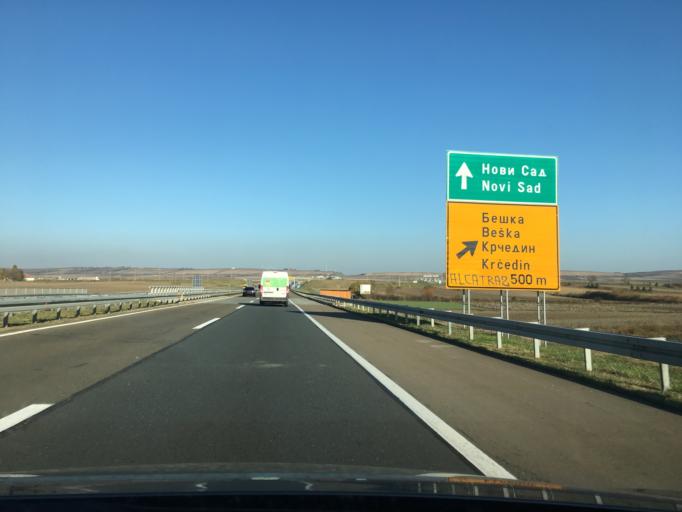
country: RS
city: Beska
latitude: 45.1287
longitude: 20.0912
